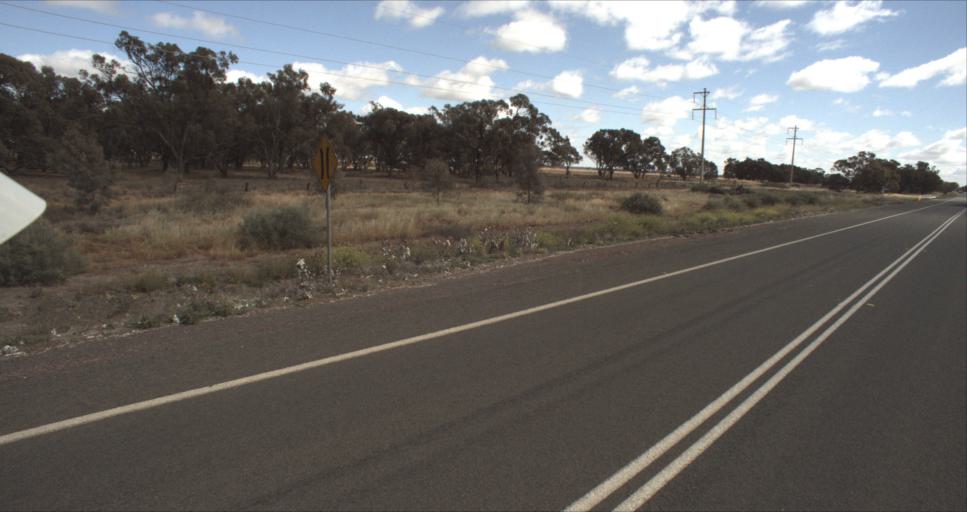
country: AU
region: New South Wales
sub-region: Murrumbidgee Shire
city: Darlington Point
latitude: -34.5756
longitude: 146.1662
